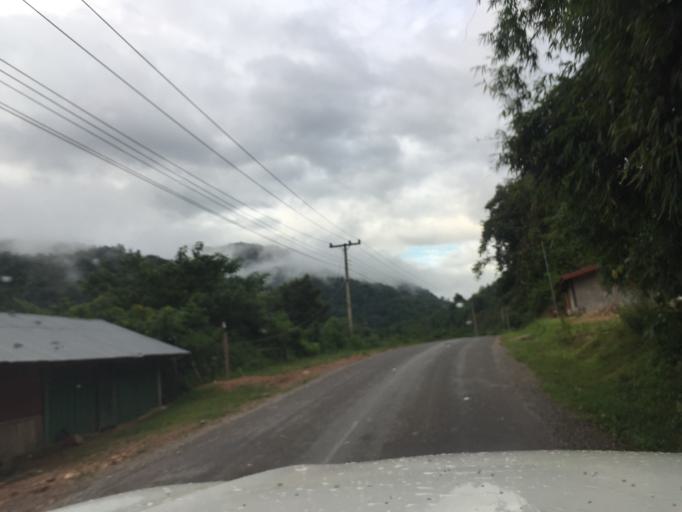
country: LA
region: Oudomxai
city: Muang La
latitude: 20.8721
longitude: 102.1338
